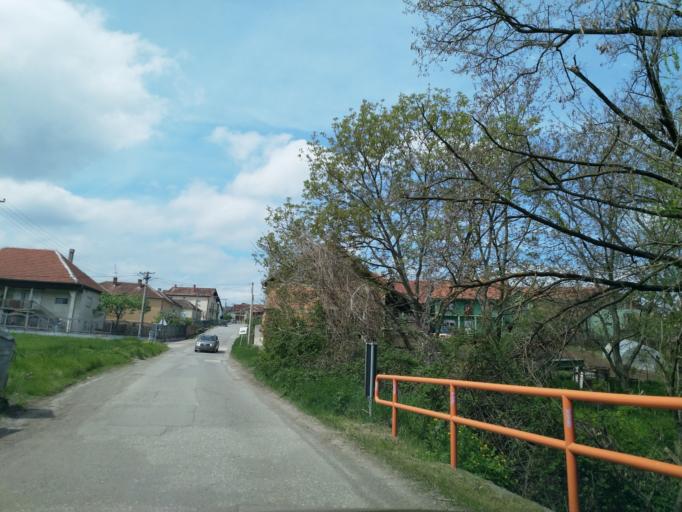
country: RS
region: Central Serbia
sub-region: Pomoravski Okrug
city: Paracin
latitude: 43.9363
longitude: 21.4935
